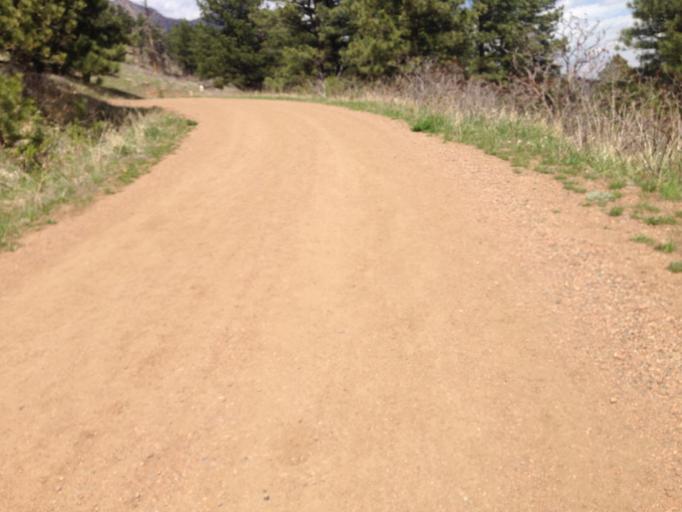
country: US
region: Colorado
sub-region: Boulder County
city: Boulder
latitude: 39.9285
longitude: -105.2735
